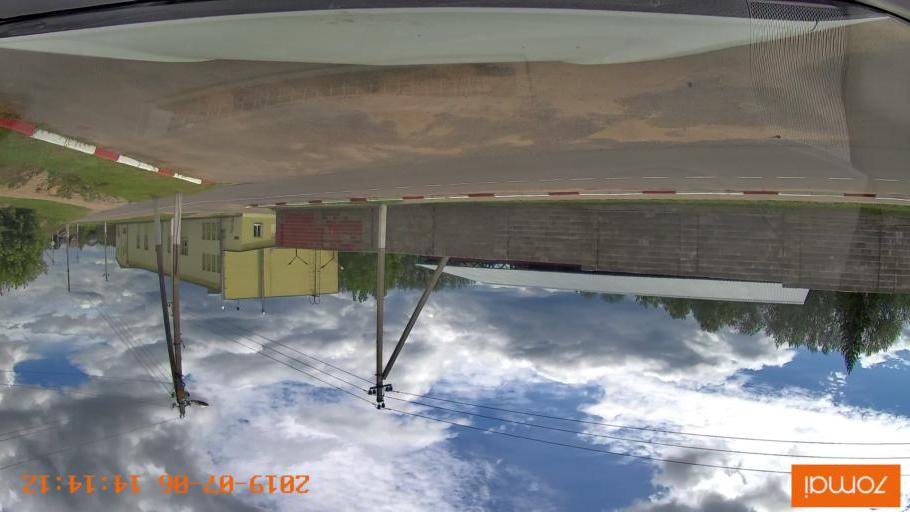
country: BY
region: Minsk
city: Ivyanyets
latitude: 53.8919
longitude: 26.7375
